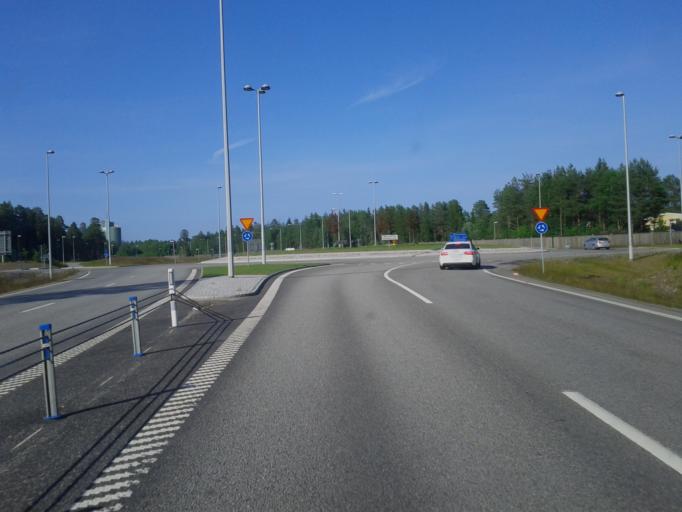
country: SE
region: Vaesterbotten
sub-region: Umea Kommun
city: Umea
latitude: 63.8054
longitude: 20.3204
